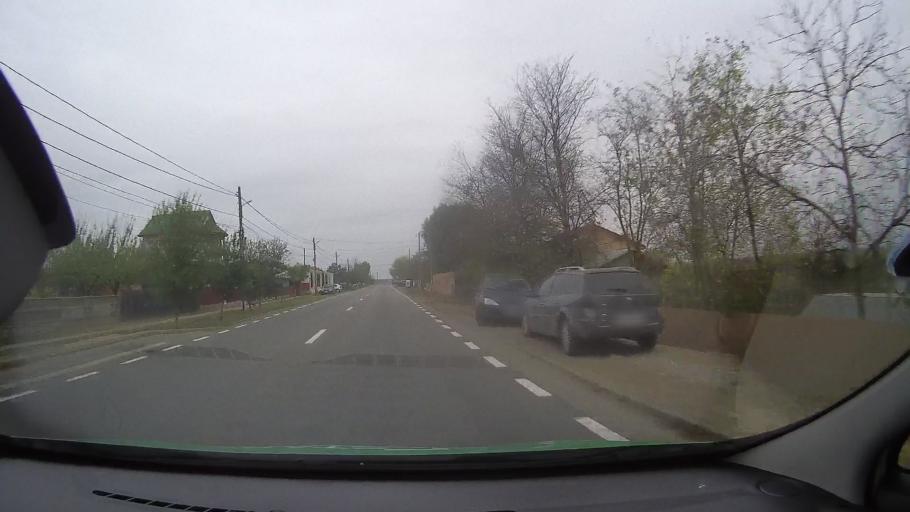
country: RO
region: Ialomita
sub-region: Comuna Slobozia
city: Slobozia
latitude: 44.5979
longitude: 27.3897
